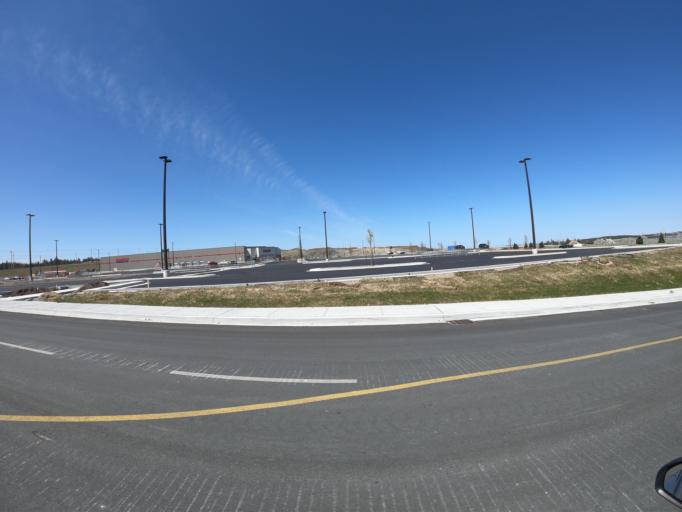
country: CA
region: Newfoundland and Labrador
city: Mount Pearl
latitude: 47.5078
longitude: -52.8329
